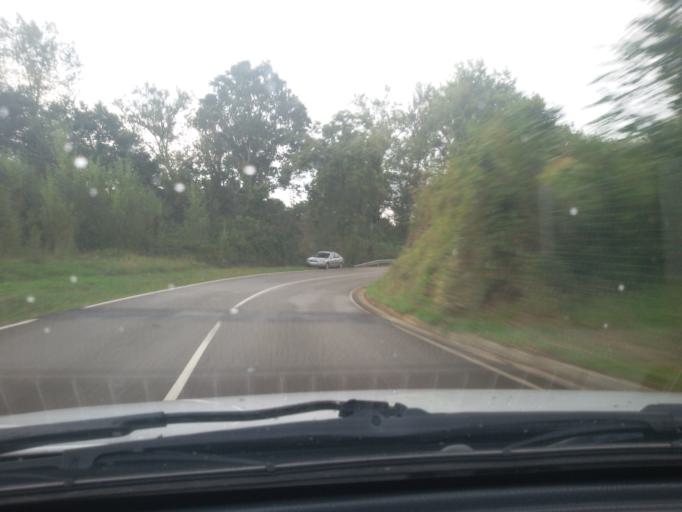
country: ES
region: Asturias
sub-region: Province of Asturias
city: Norena
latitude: 43.3719
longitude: -5.7368
